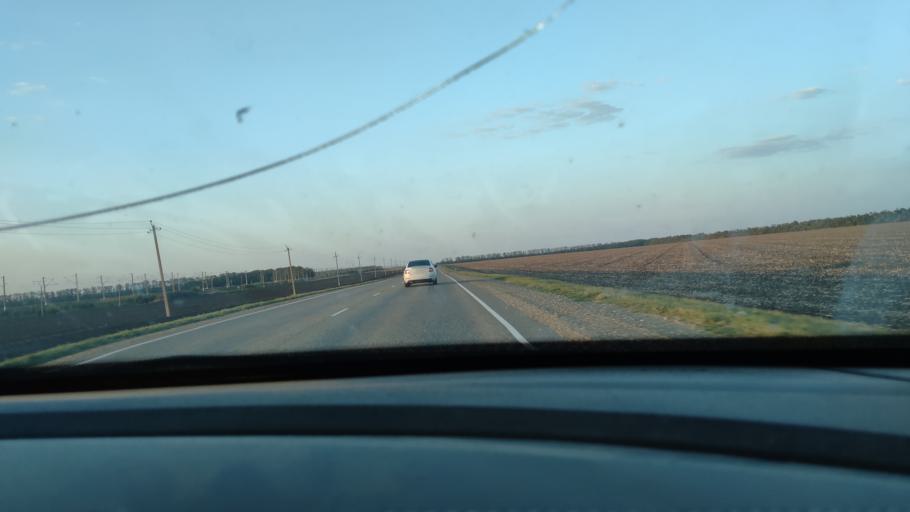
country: RU
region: Krasnodarskiy
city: Novominskaya
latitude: 46.3621
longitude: 38.9692
